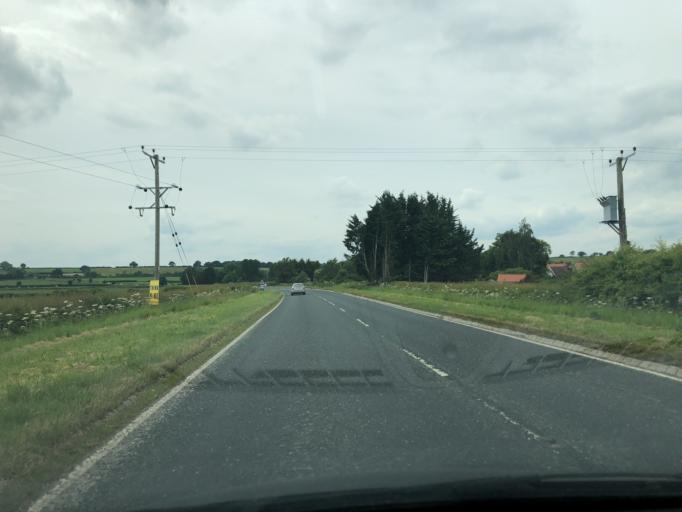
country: GB
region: England
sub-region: North Yorkshire
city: Pickering
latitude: 54.2631
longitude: -0.8240
